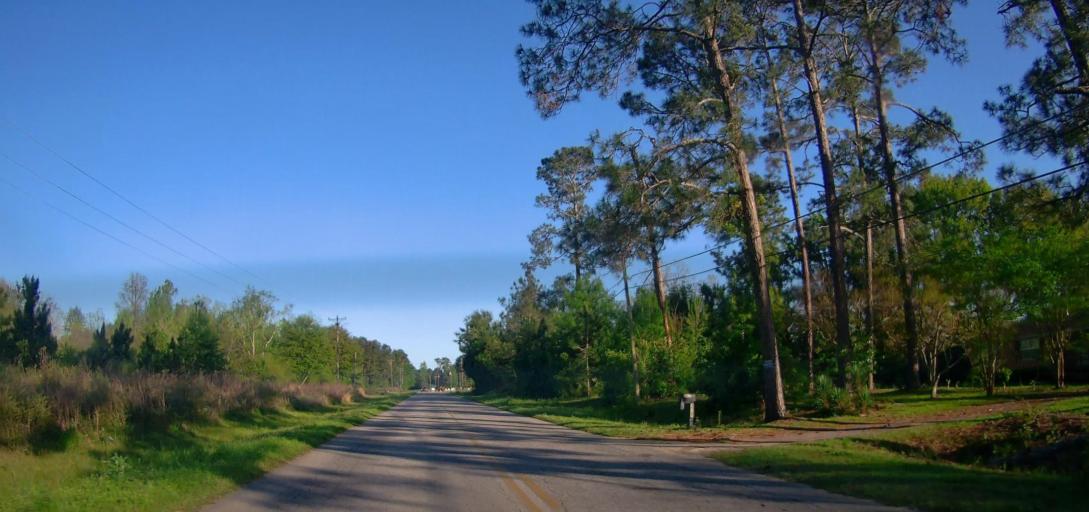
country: US
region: Georgia
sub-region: Ben Hill County
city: Fitzgerald
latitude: 31.7048
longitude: -83.2288
